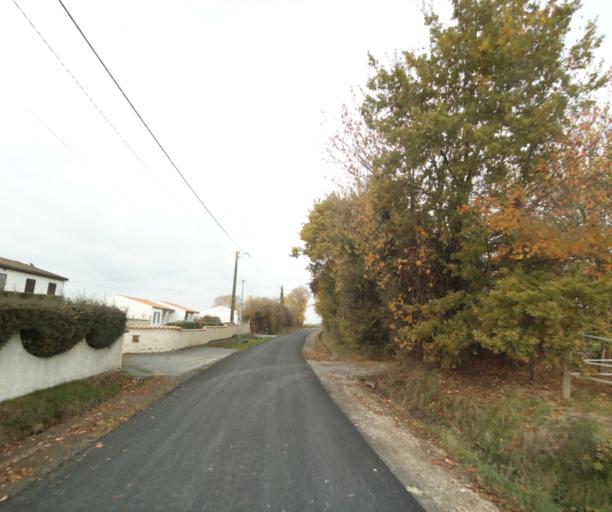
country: FR
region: Poitou-Charentes
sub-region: Departement de la Charente-Maritime
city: Saint-Georges-des-Coteaux
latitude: 45.7703
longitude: -0.7154
